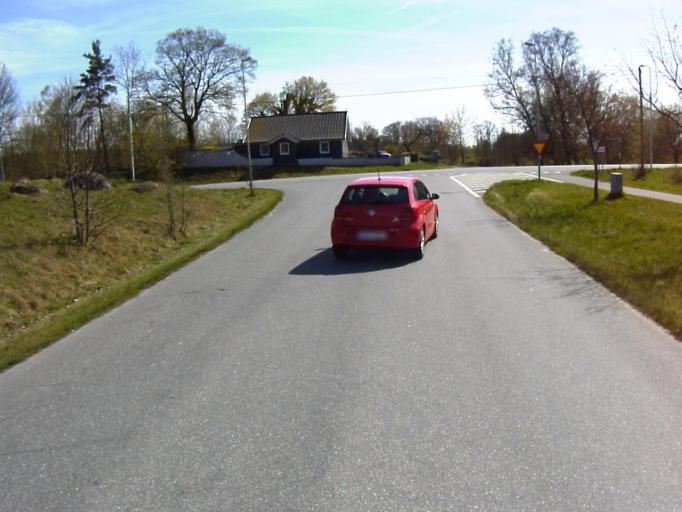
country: SE
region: Skane
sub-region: Kristianstads Kommun
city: Onnestad
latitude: 55.9951
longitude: 14.0654
